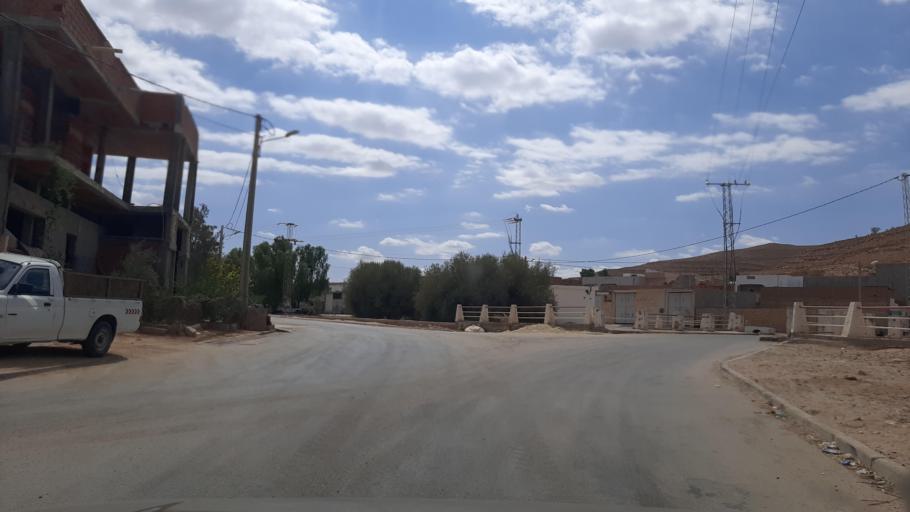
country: TN
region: Tataouine
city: Tataouine
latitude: 32.9270
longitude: 10.4583
